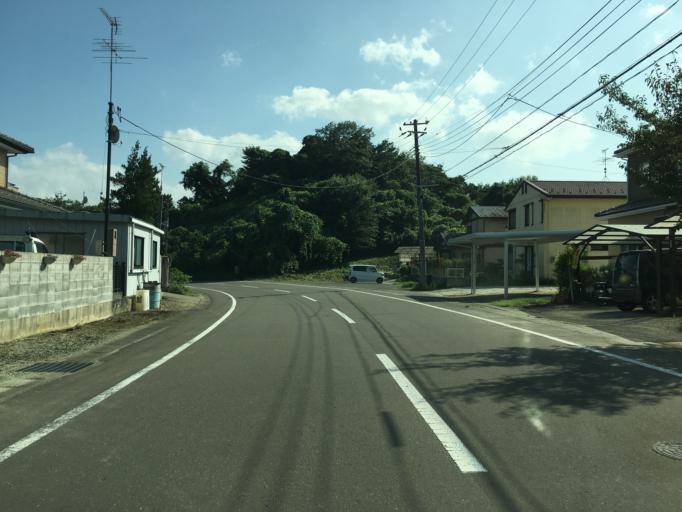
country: JP
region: Miyagi
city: Marumori
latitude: 37.9407
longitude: 140.7719
